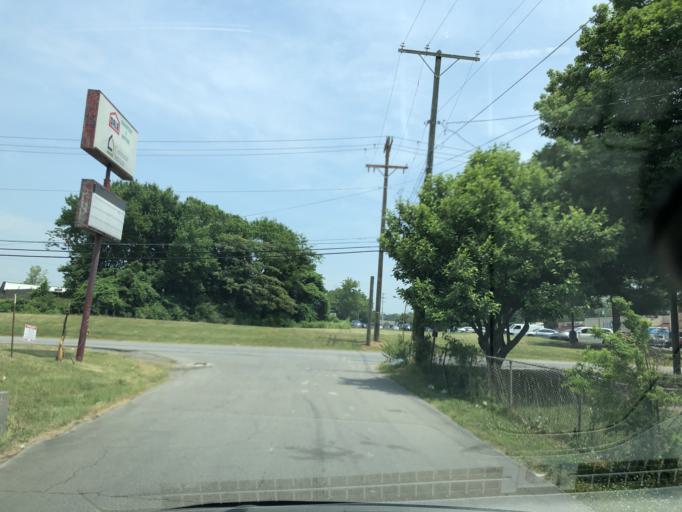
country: US
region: Tennessee
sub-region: Davidson County
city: Oak Hill
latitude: 36.0678
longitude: -86.6832
